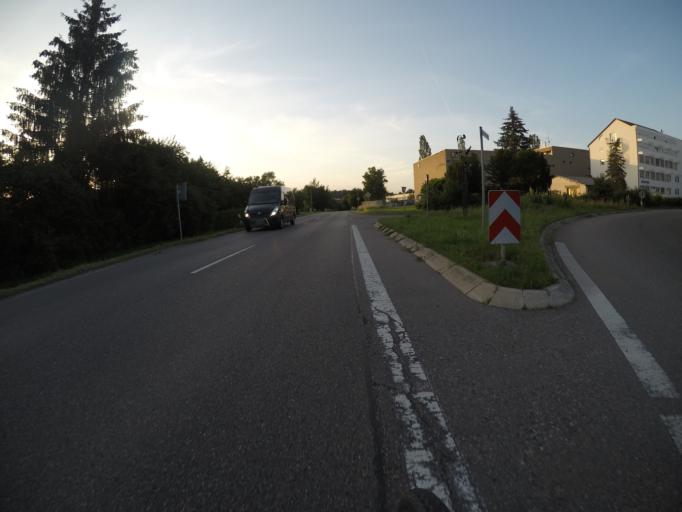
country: DE
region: Baden-Wuerttemberg
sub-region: Regierungsbezirk Stuttgart
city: Steinenbronn
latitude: 48.6638
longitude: 9.1239
